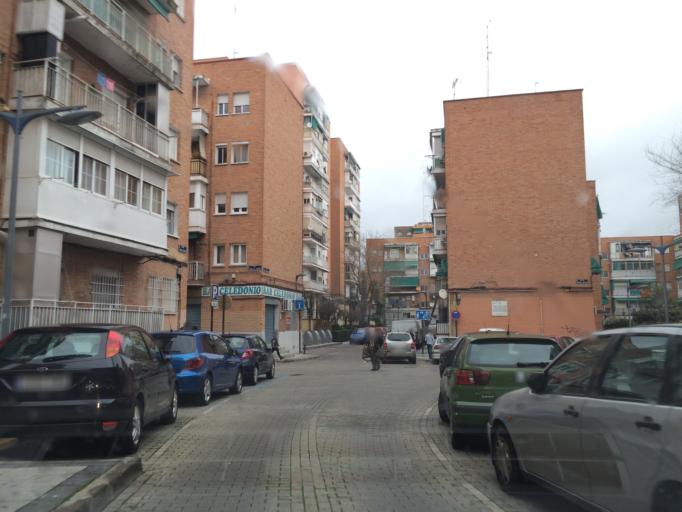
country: ES
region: Madrid
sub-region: Provincia de Madrid
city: Alcorcon
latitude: 40.3478
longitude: -3.8213
